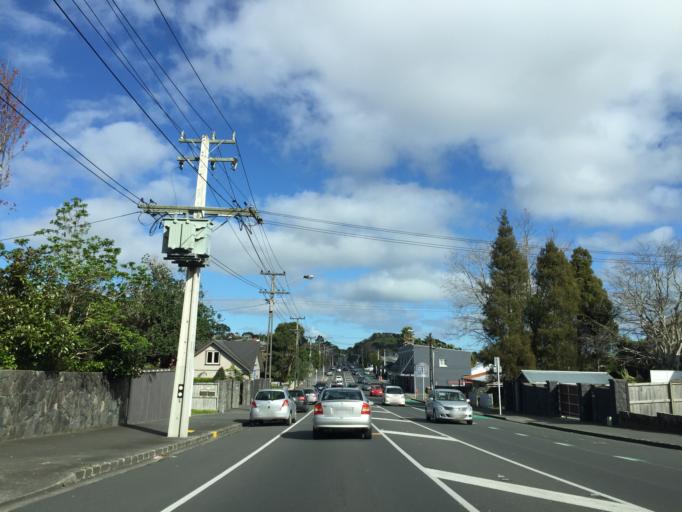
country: NZ
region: Auckland
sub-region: Auckland
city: Auckland
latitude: -36.8909
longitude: 174.7596
